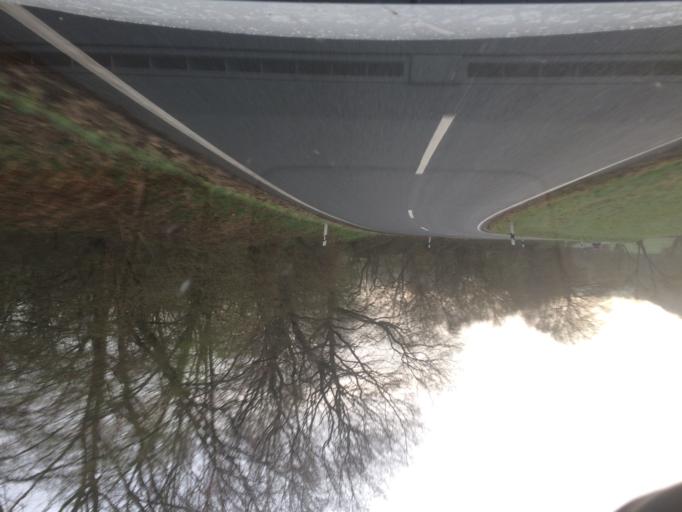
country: DE
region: Thuringia
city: Weissenborn-Luderode
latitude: 51.5425
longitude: 10.3893
